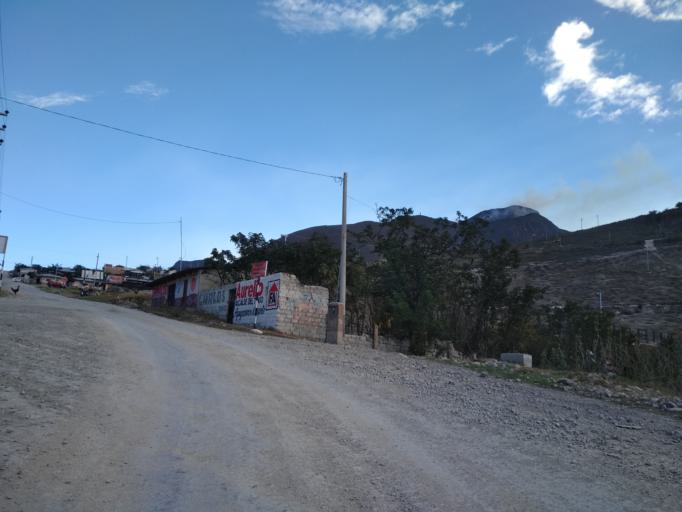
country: PE
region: Amazonas
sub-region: Provincia de Luya
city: Tingo
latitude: -6.3725
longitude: -77.9125
